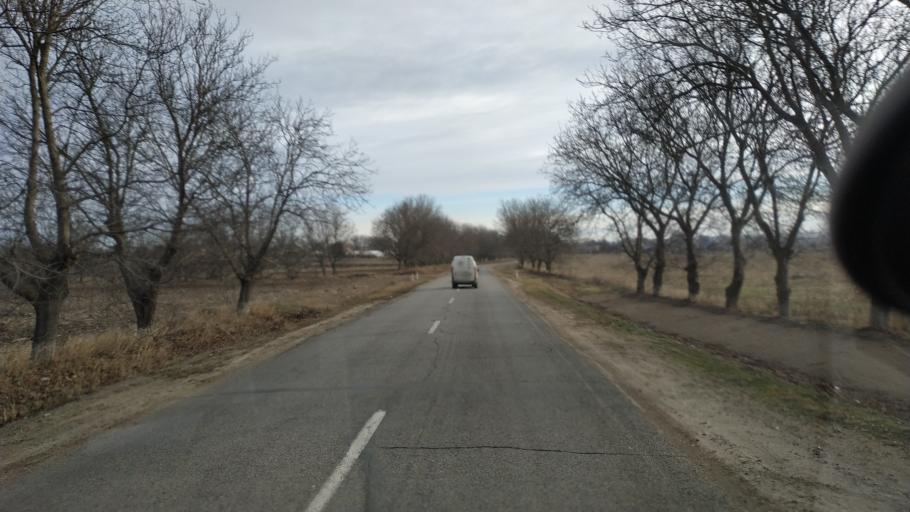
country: MD
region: Chisinau
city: Vadul lui Voda
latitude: 47.1567
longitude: 29.1079
